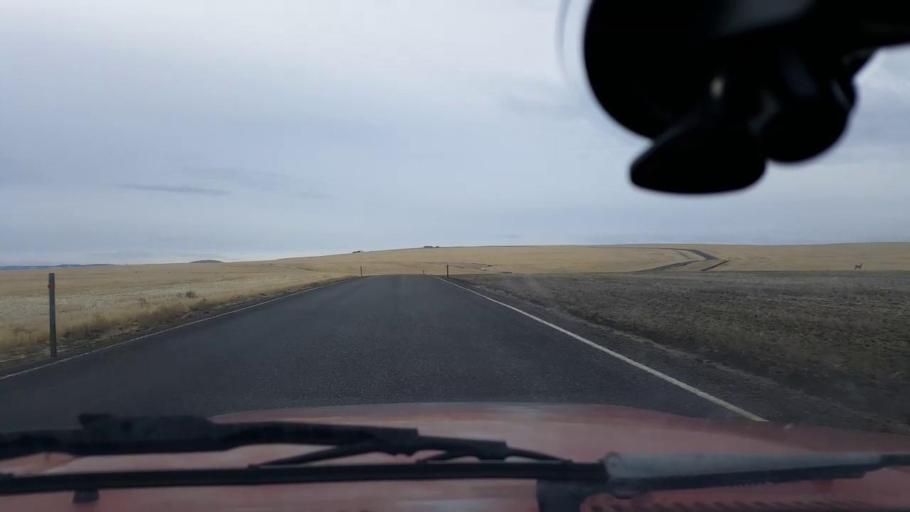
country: US
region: Washington
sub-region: Asotin County
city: Clarkston Heights-Vineland
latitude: 46.3449
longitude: -117.2443
